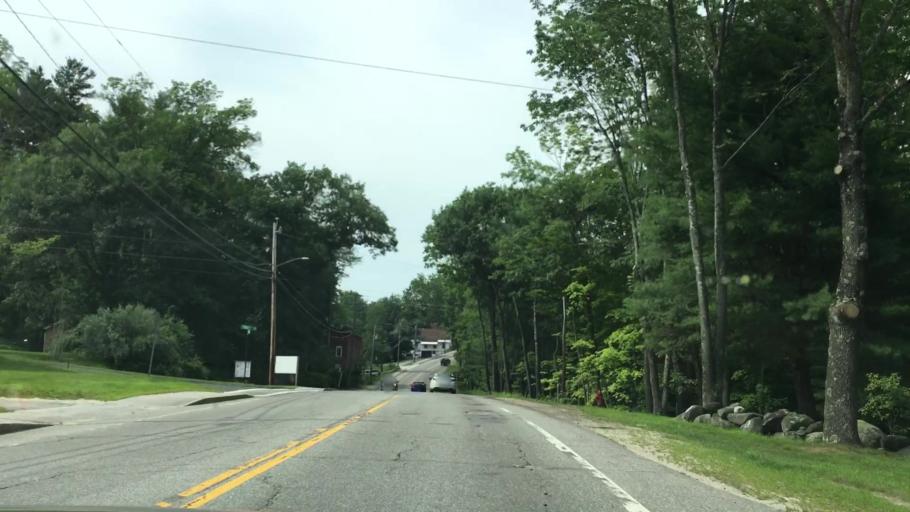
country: US
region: New Hampshire
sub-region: Hillsborough County
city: Antrim
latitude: 43.0247
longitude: -71.9364
